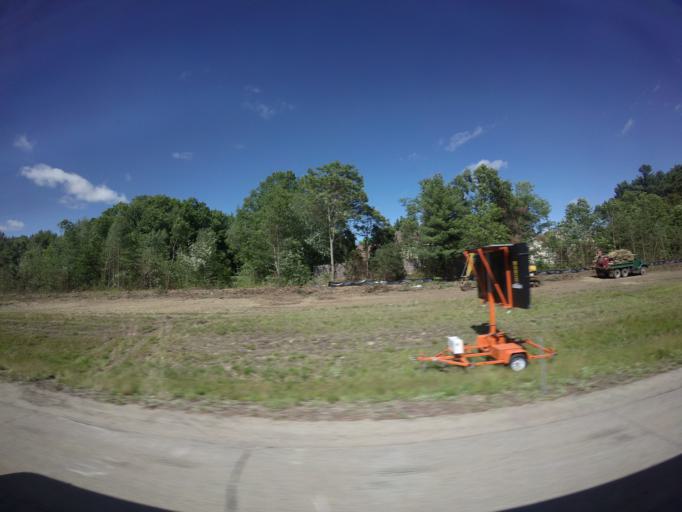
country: US
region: New Hampshire
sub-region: Rockingham County
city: Auburn
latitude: 42.9451
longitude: -71.3907
